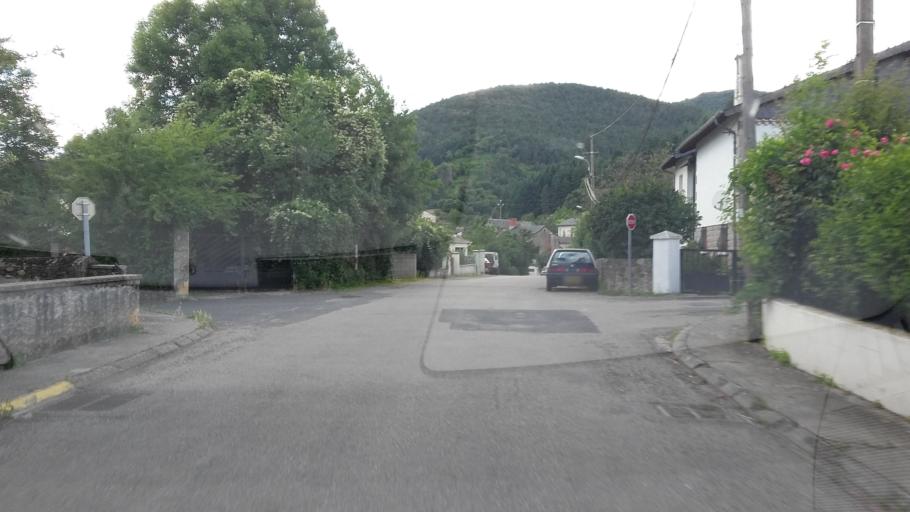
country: FR
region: Languedoc-Roussillon
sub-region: Departement de la Lozere
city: Meyrueis
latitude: 44.0254
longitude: 3.3584
